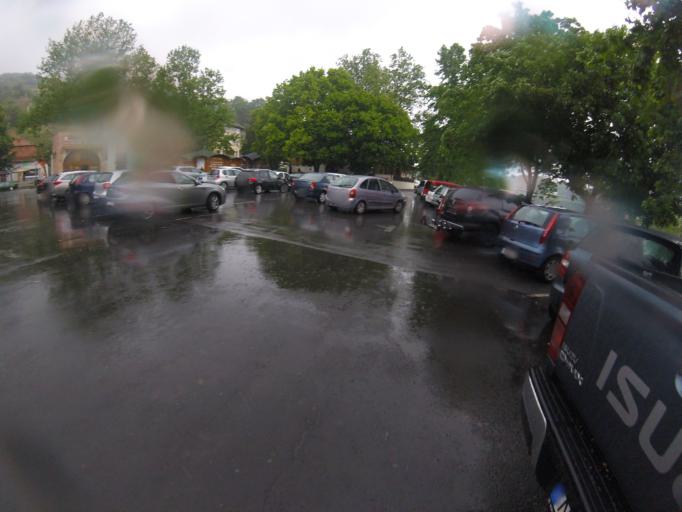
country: HU
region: Borsod-Abauj-Zemplen
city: Tokaj
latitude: 48.1197
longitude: 21.4132
